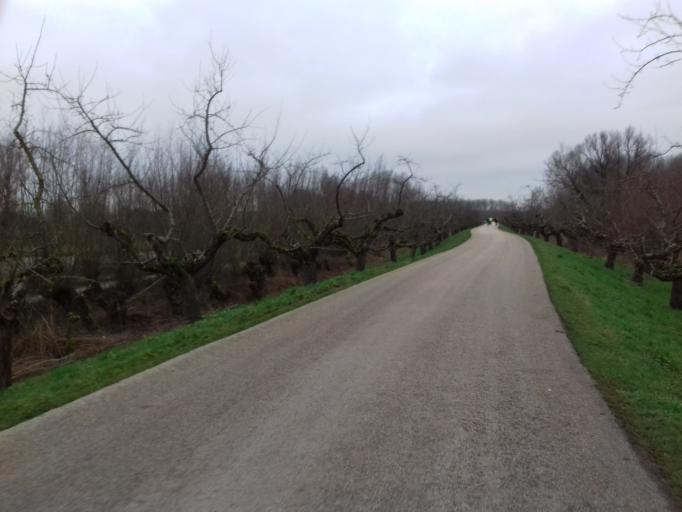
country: NL
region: Gelderland
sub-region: Gemeente Geldermalsen
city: Geldermalsen
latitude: 51.8947
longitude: 5.2429
